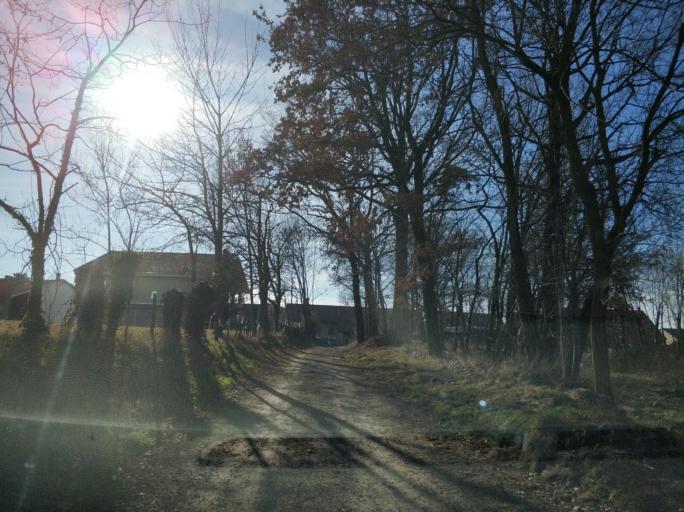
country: IT
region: Piedmont
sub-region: Provincia di Torino
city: San Carlo Canavese
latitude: 45.2530
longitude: 7.6073
